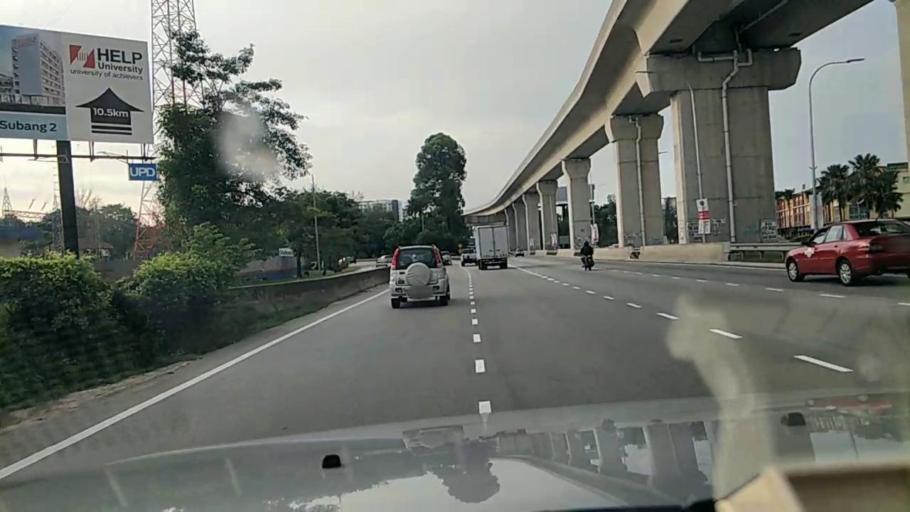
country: MY
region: Selangor
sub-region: Petaling
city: Petaling Jaya
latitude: 3.0969
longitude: 101.5899
